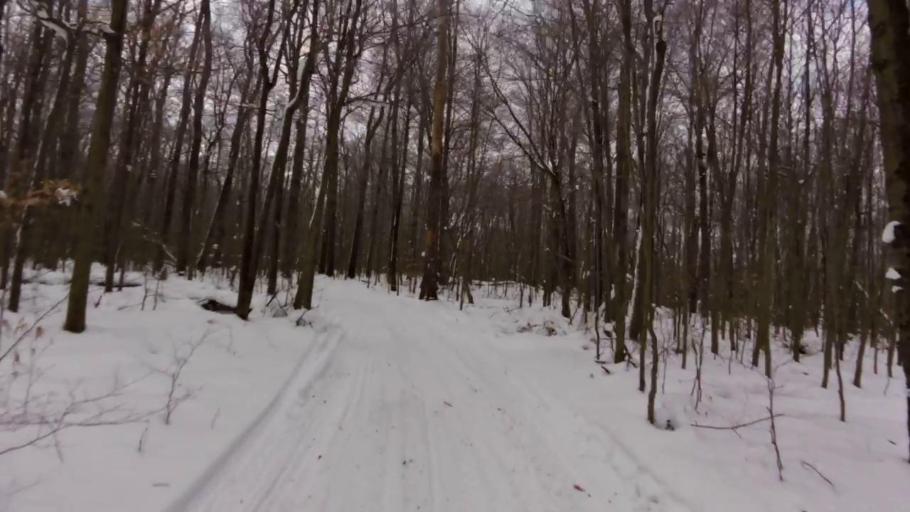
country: US
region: Pennsylvania
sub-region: McKean County
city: Bradford
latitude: 42.0320
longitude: -78.7449
